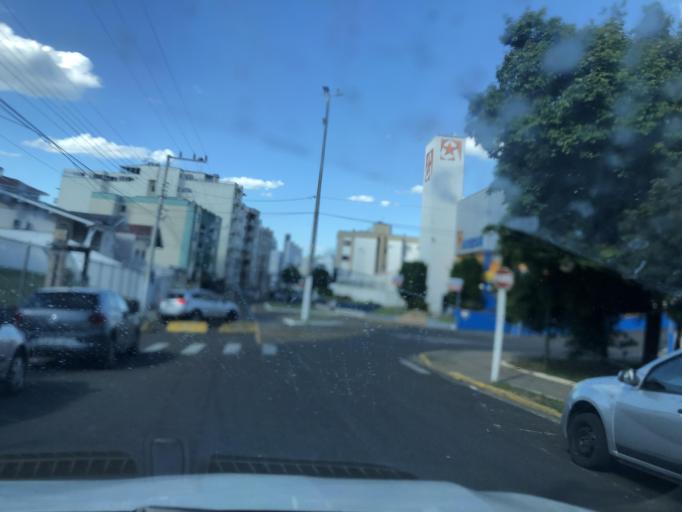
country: BR
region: Santa Catarina
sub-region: Lages
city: Lages
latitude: -27.8123
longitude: -50.3227
